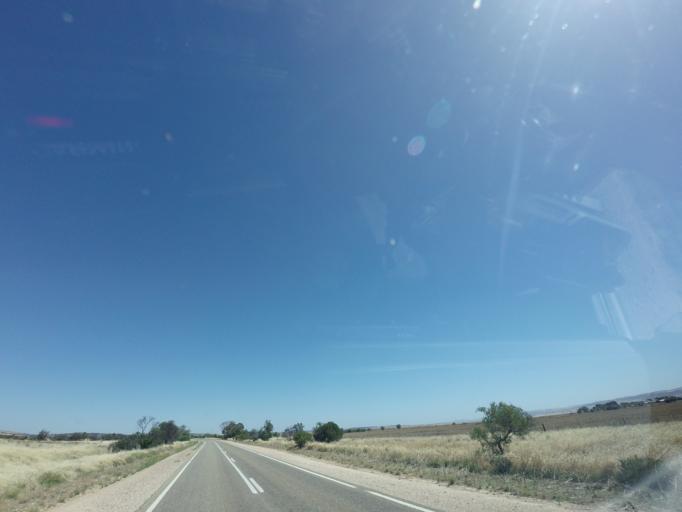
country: AU
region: South Australia
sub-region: Peterborough
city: Peterborough
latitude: -32.8781
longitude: 138.7397
